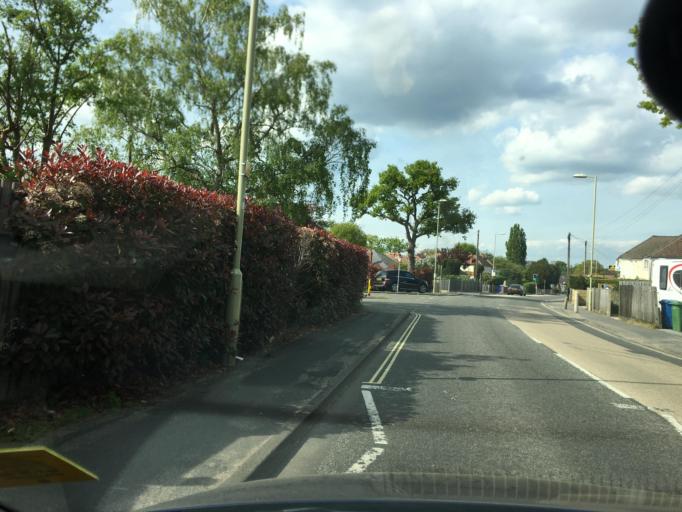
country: GB
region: England
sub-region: Hampshire
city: Farnborough
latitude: 51.3000
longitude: -0.7780
